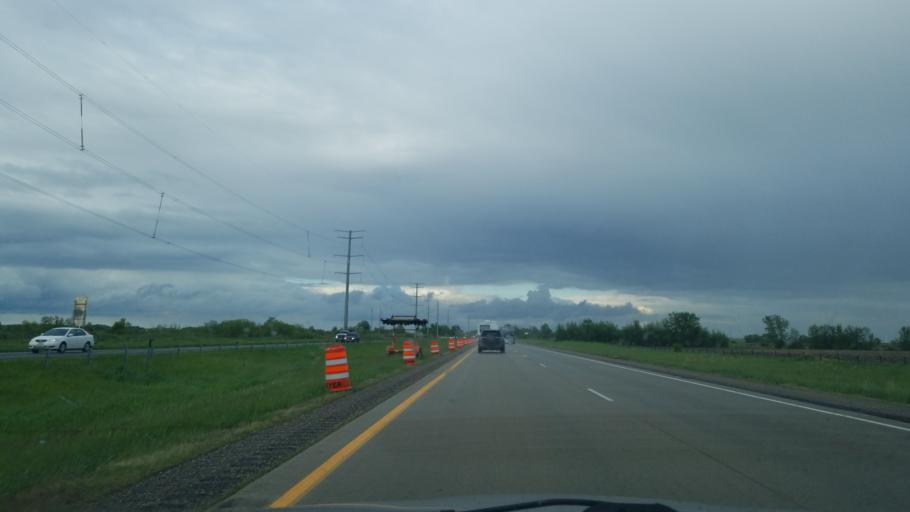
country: US
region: Minnesota
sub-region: Douglas County
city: Osakis
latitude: 45.8325
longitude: -95.1715
